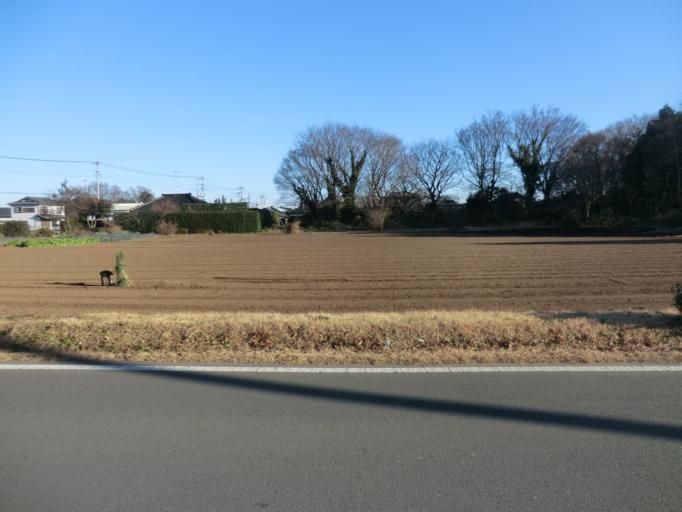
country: JP
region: Ibaraki
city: Mitsukaido
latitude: 35.9785
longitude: 139.9583
